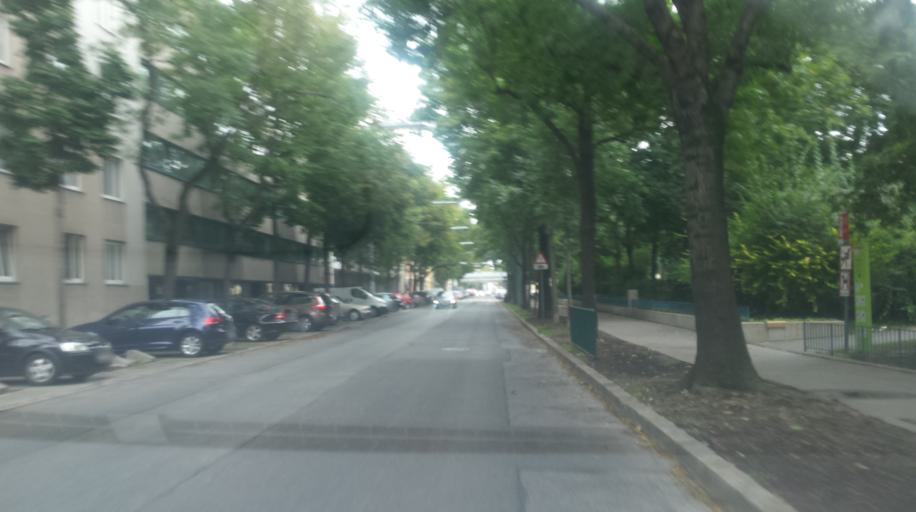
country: AT
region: Vienna
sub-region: Wien Stadt
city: Vienna
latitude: 48.1714
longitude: 16.4143
